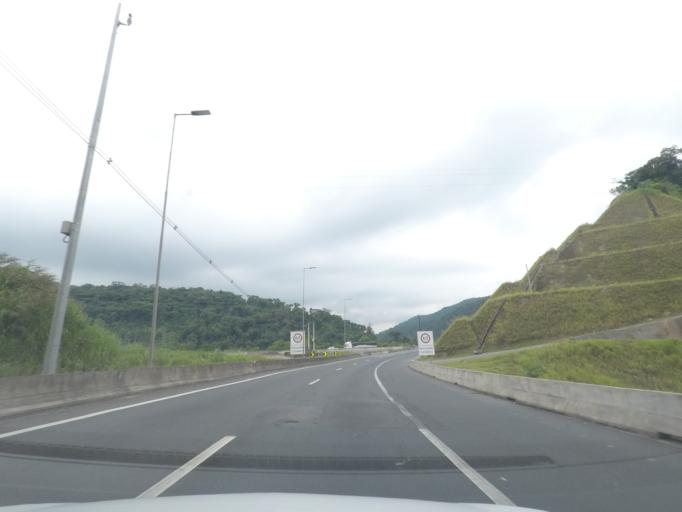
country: BR
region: Sao Paulo
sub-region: Miracatu
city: Miracatu
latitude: -24.1199
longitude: -47.2691
